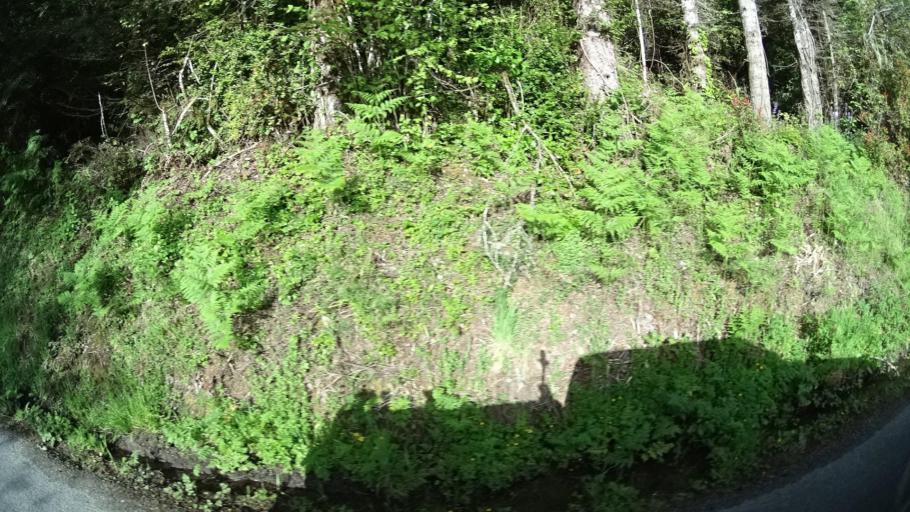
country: US
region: California
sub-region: Humboldt County
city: Blue Lake
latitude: 40.8812
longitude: -124.0171
